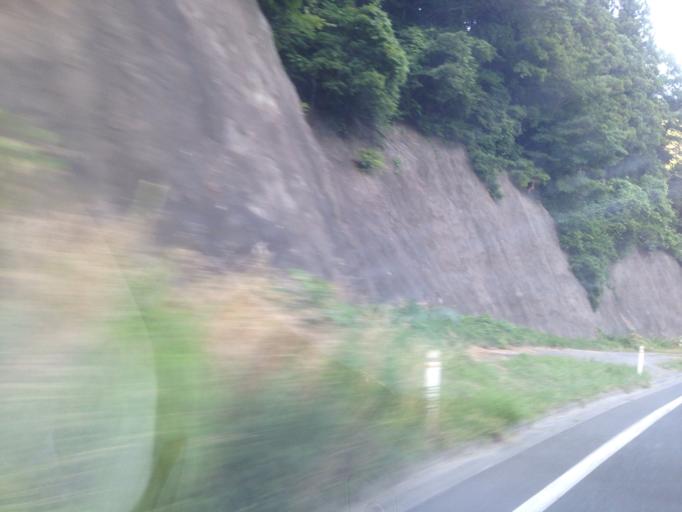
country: JP
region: Iwate
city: Otsuchi
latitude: 39.3907
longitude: 141.8675
